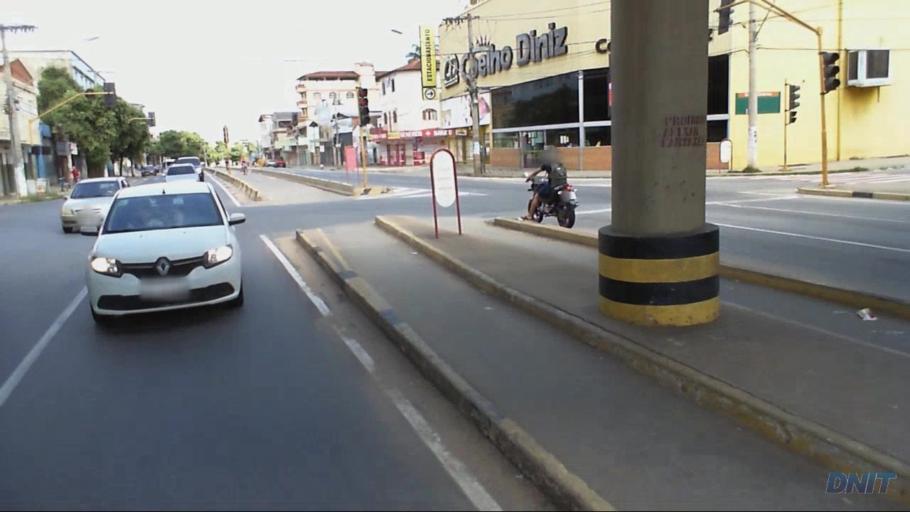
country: BR
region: Minas Gerais
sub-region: Governador Valadares
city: Governador Valadares
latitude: -18.8784
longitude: -41.9619
